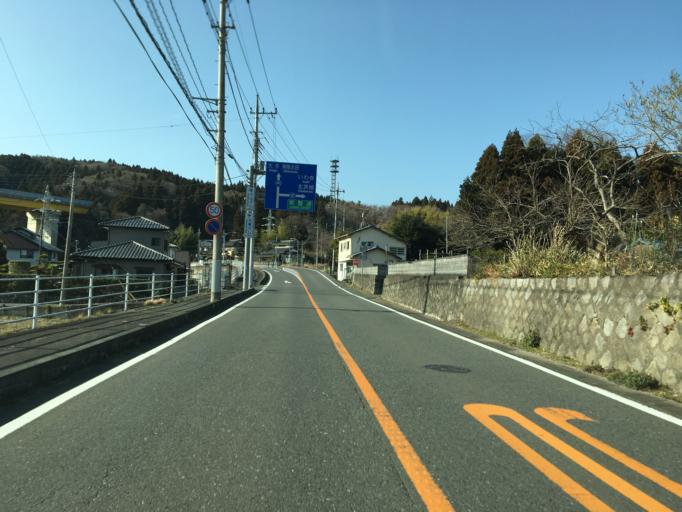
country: JP
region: Ibaraki
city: Takahagi
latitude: 36.7236
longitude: 140.6732
